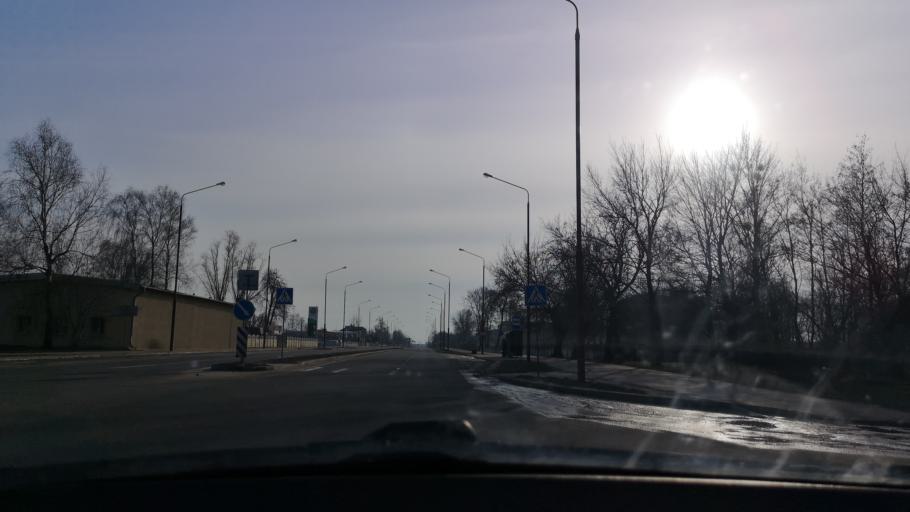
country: BY
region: Brest
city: Brest
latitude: 52.1239
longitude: 23.6718
